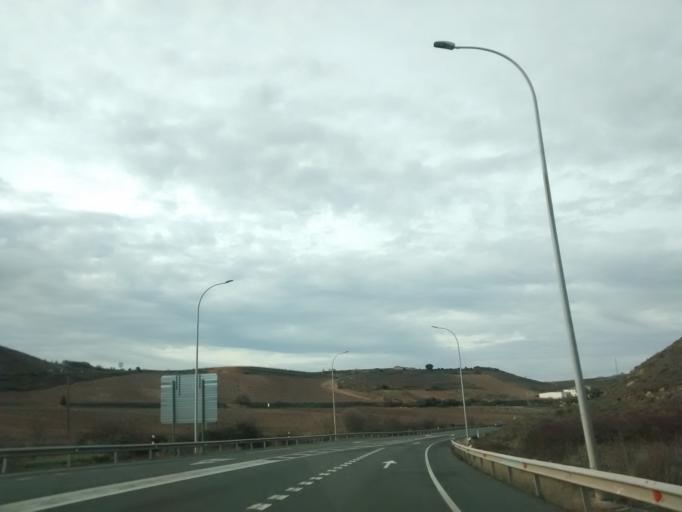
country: ES
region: La Rioja
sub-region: Provincia de La Rioja
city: Cenicero
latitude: 42.4718
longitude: -2.6405
